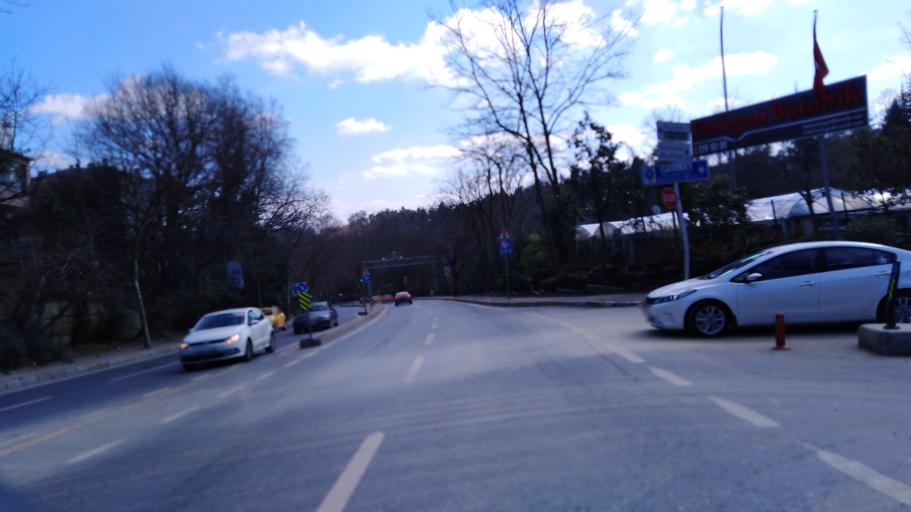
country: TR
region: Istanbul
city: Sisli
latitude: 41.1111
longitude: 29.0468
